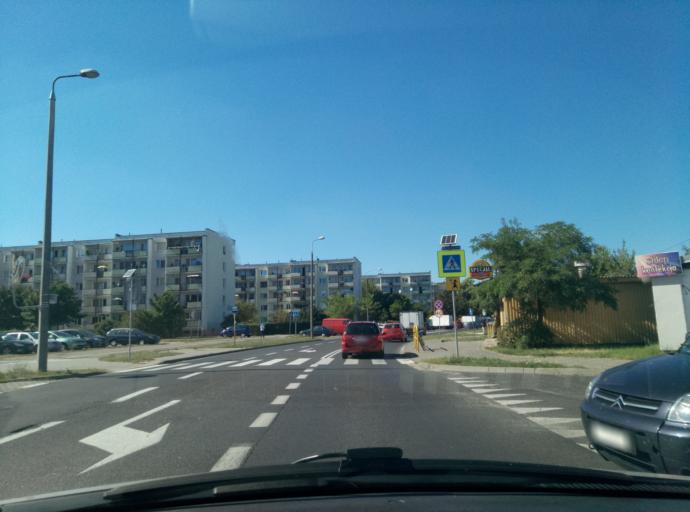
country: PL
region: Kujawsko-Pomorskie
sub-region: Torun
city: Torun
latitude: 53.0344
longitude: 18.5989
